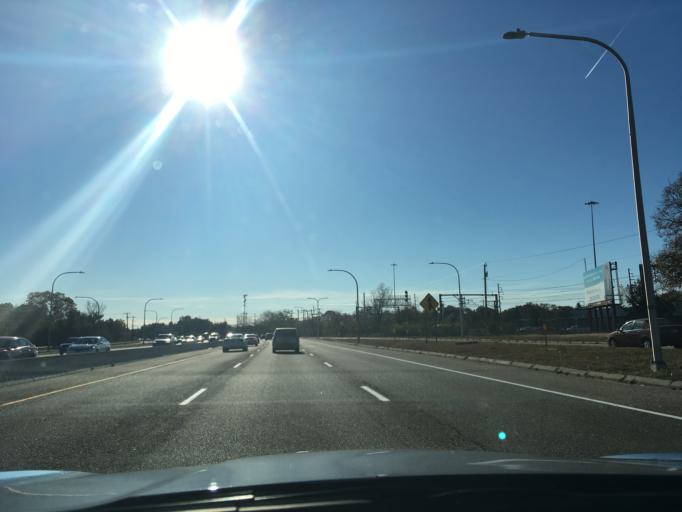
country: US
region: Rhode Island
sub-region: Providence County
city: Providence
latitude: 41.8540
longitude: -71.4082
